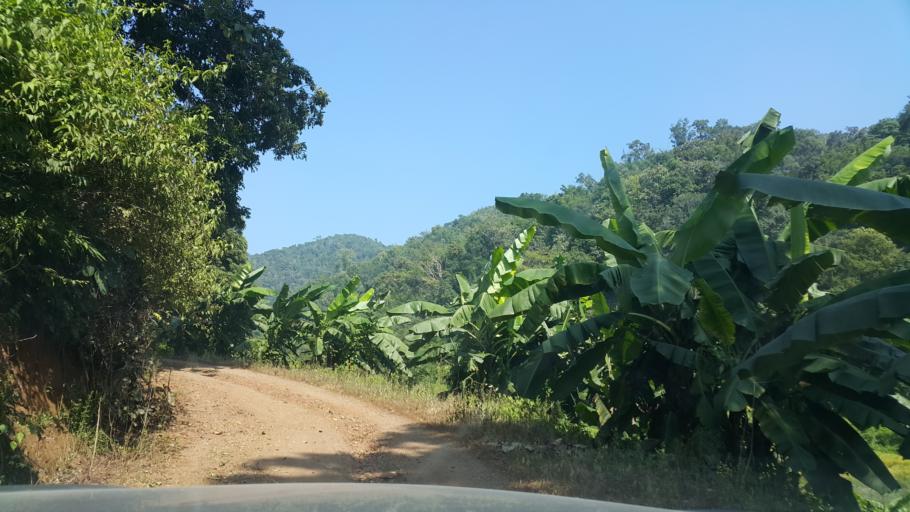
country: TH
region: Chiang Mai
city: Samoeng
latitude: 18.9409
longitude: 98.6191
